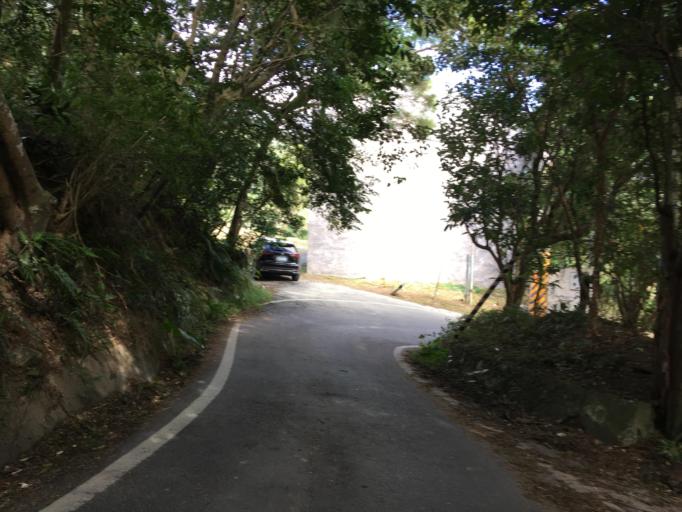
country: TW
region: Taiwan
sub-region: Yilan
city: Yilan
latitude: 24.8399
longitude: 121.7772
